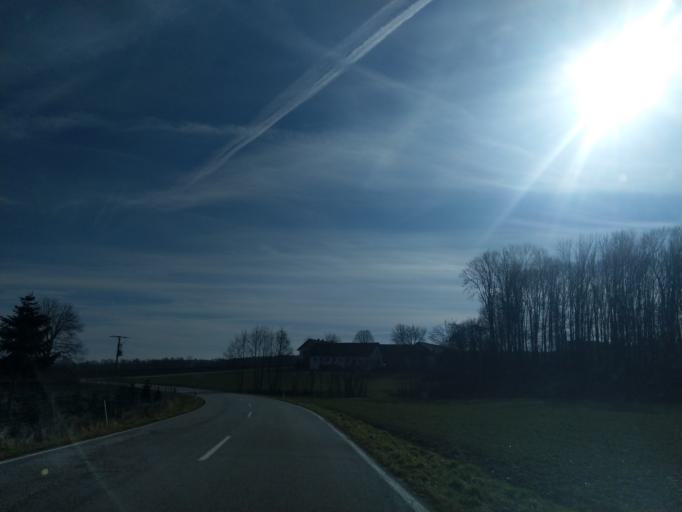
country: DE
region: Bavaria
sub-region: Lower Bavaria
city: Buchhofen
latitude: 48.6691
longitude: 12.9269
